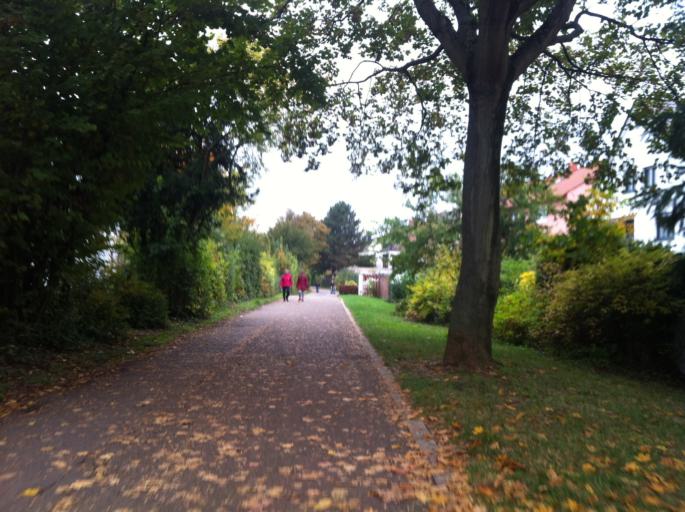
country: DE
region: Rheinland-Pfalz
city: Mainz
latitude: 49.9827
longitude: 8.2784
